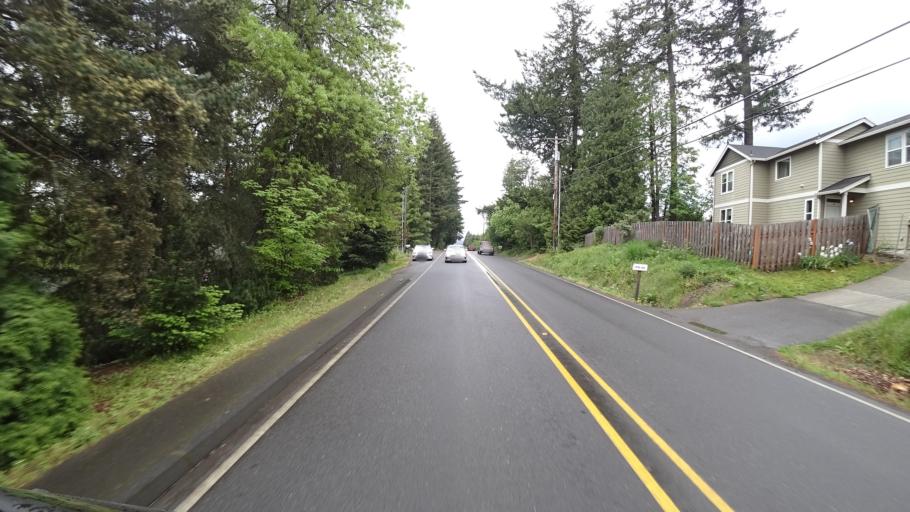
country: US
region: Oregon
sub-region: Washington County
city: West Haven
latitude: 45.5290
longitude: -122.7683
